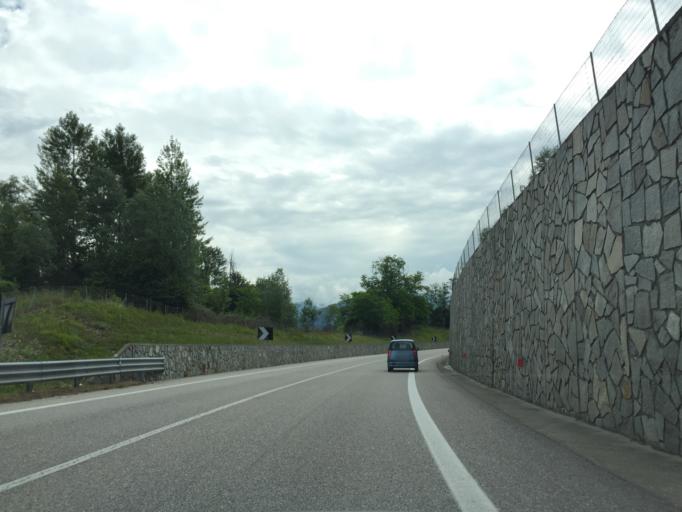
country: IT
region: Veneto
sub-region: Provincia di Belluno
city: Feltre
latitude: 46.0117
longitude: 11.8968
